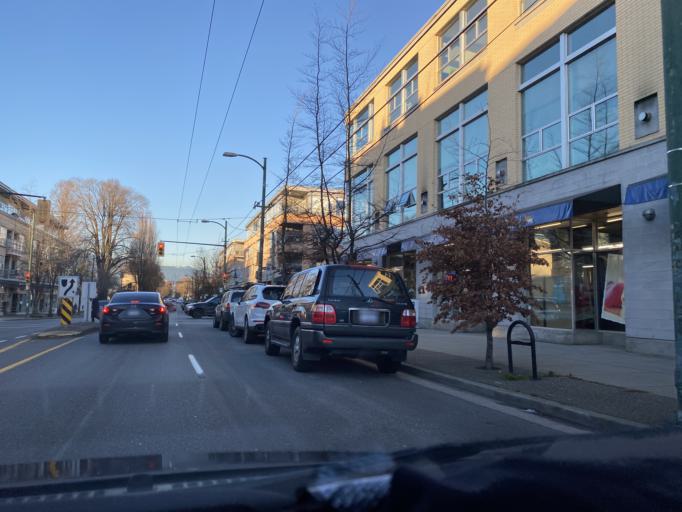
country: CA
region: British Columbia
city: West End
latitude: 49.2615
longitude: -123.1530
